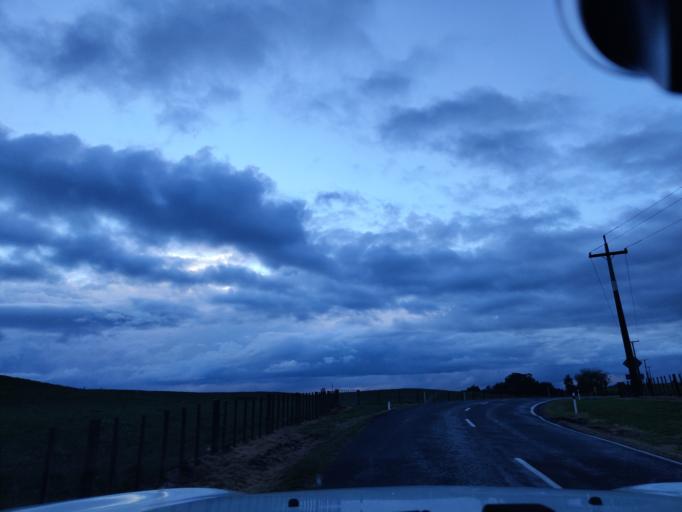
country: NZ
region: Waikato
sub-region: South Waikato District
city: Tokoroa
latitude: -38.1835
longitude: 175.7870
